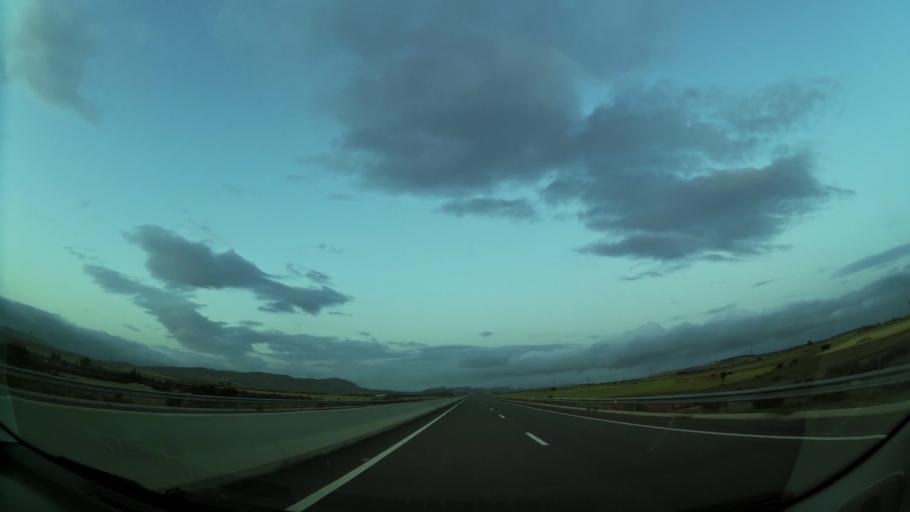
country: MA
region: Oriental
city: El Aioun
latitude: 34.6262
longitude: -2.5262
